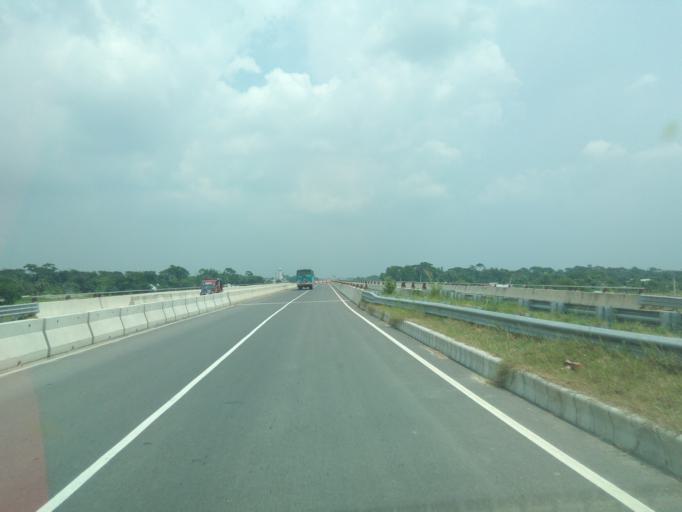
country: BD
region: Dhaka
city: Char Bhadrasan
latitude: 23.3998
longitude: 90.2124
